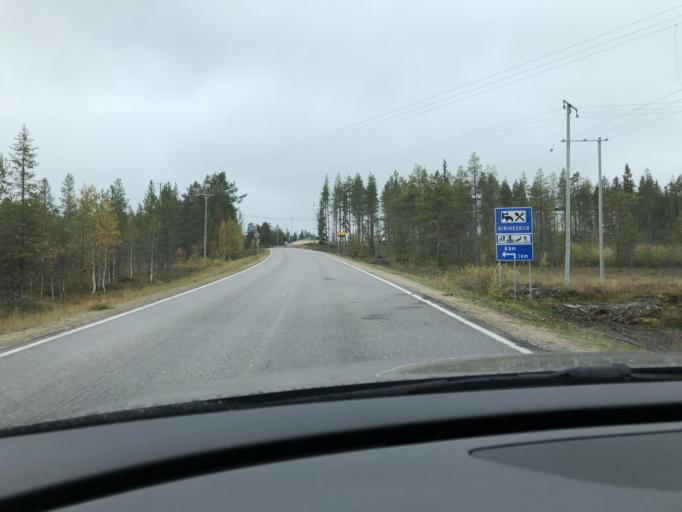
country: FI
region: Lapland
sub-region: Itae-Lappi
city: Posio
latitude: 66.1201
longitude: 28.1828
